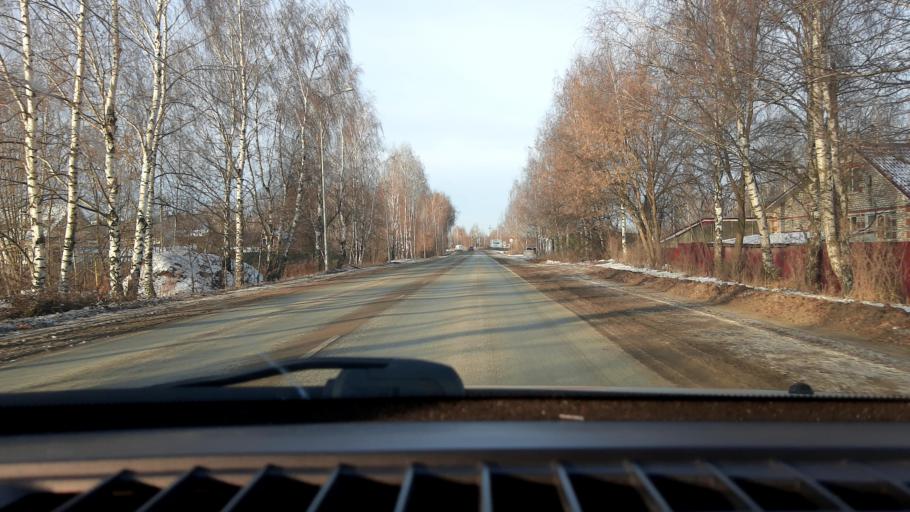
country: RU
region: Nizjnij Novgorod
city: Bor
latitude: 56.3806
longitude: 44.0406
